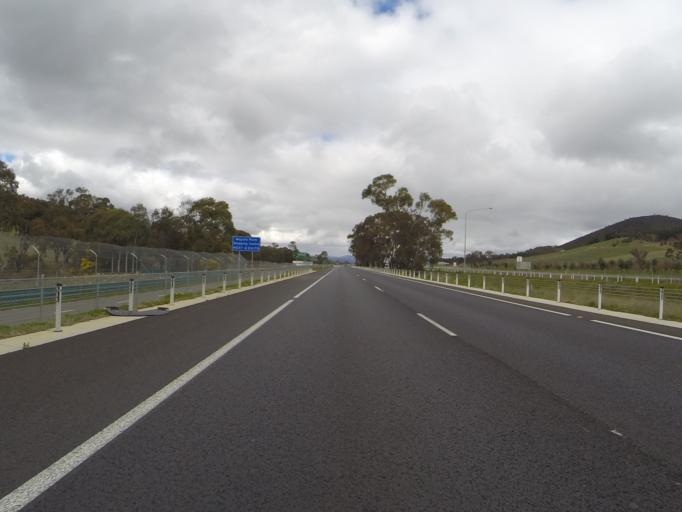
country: AU
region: Australian Capital Territory
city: Canberra
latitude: -35.2243
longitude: 149.1963
